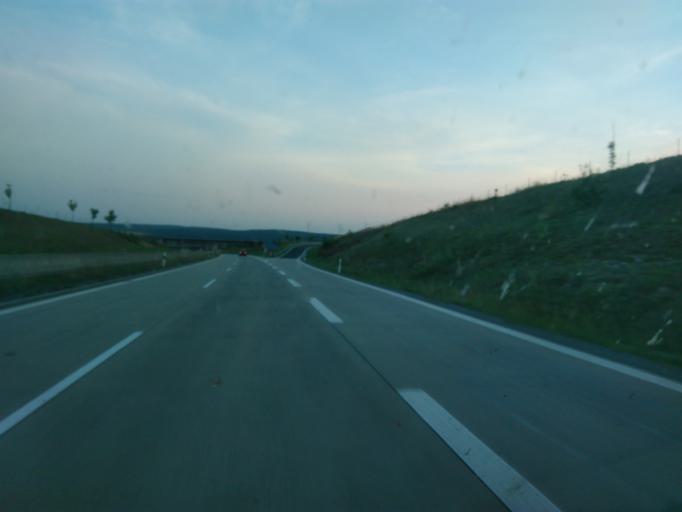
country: DE
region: Bavaria
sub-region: Regierungsbezirk Unterfranken
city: Strahlungen
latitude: 50.2632
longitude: 10.2211
